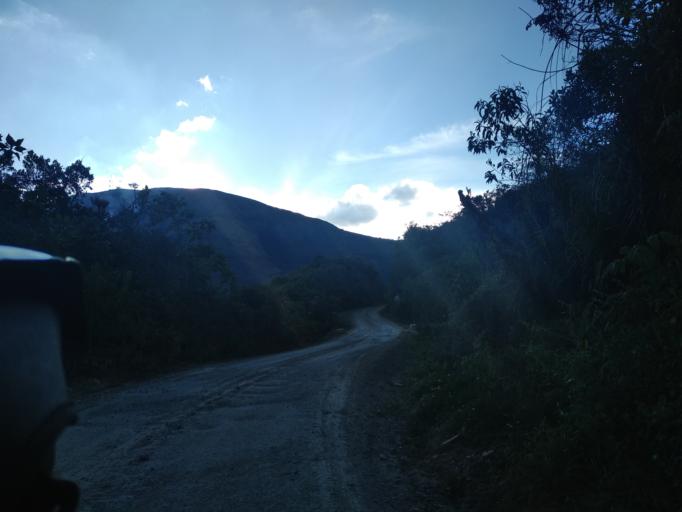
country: PE
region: Amazonas
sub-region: Provincia de Chachapoyas
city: Montevideo
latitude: -6.7197
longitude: -77.8653
